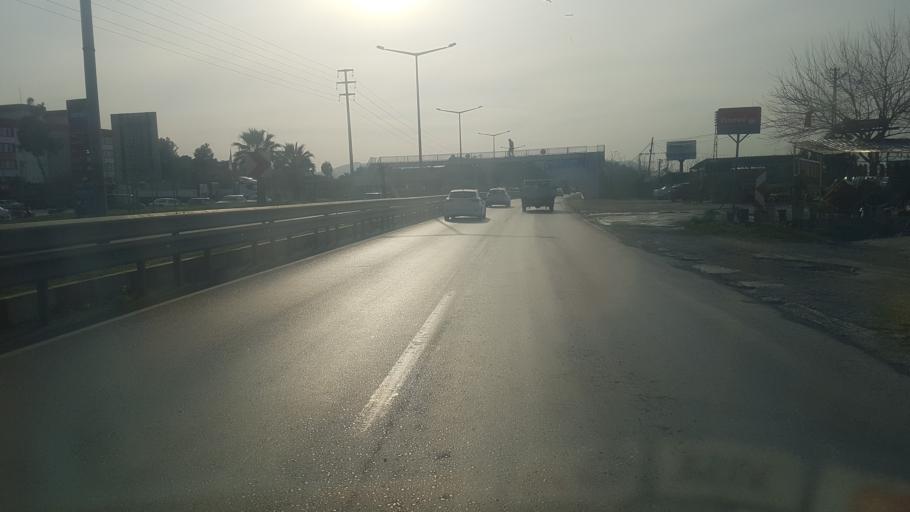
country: TR
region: Osmaniye
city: Toprakkale
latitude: 37.0528
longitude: 36.1553
